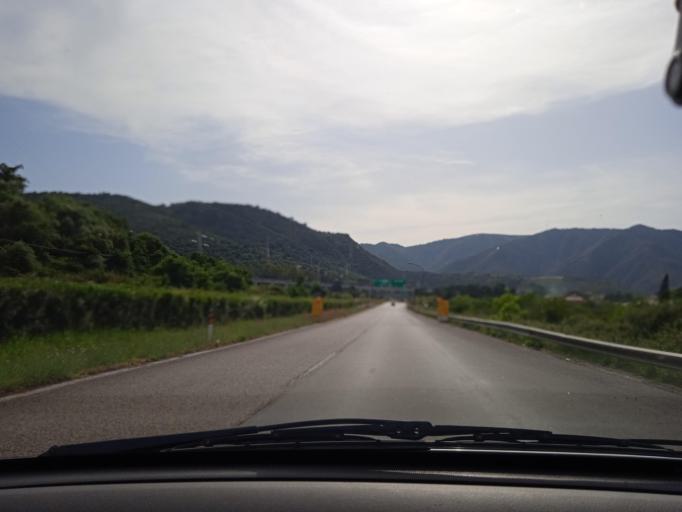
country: IT
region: Sicily
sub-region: Messina
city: Falcone
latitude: 38.1139
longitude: 15.0794
